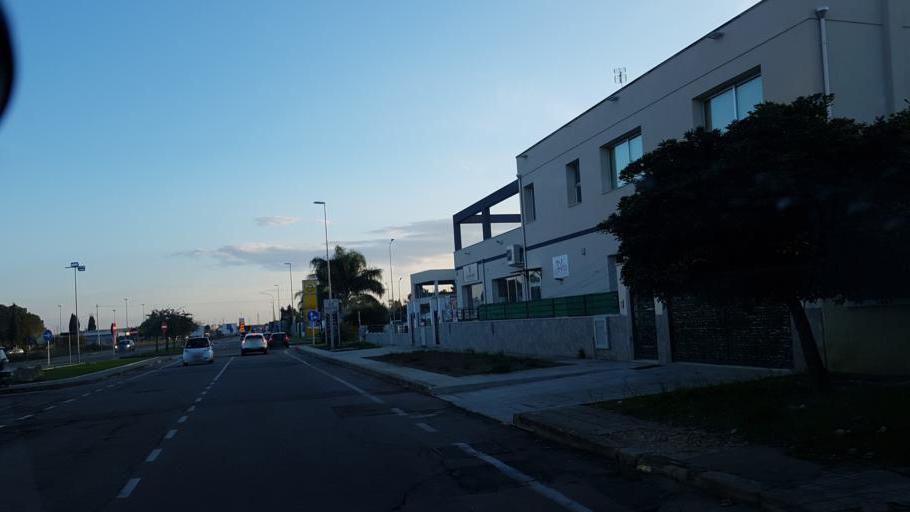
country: IT
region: Apulia
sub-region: Provincia di Lecce
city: Giorgilorio
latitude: 40.3798
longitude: 18.1397
